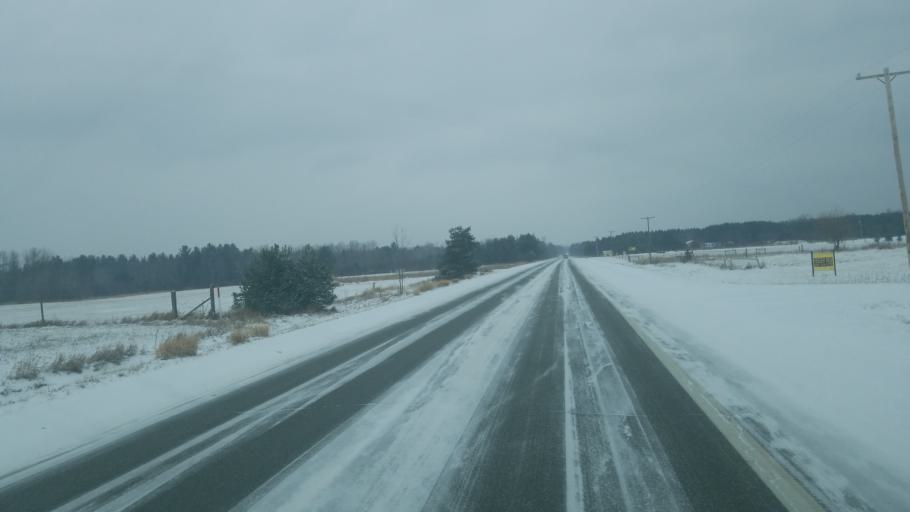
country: US
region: Michigan
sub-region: Osceola County
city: Evart
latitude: 43.9301
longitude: -85.1484
